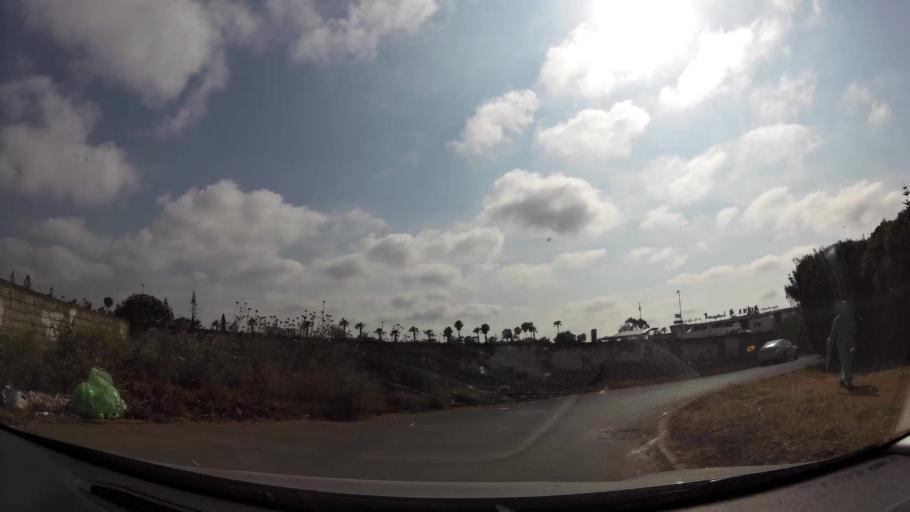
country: MA
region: Rabat-Sale-Zemmour-Zaer
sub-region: Rabat
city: Rabat
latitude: 33.9692
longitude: -6.8626
